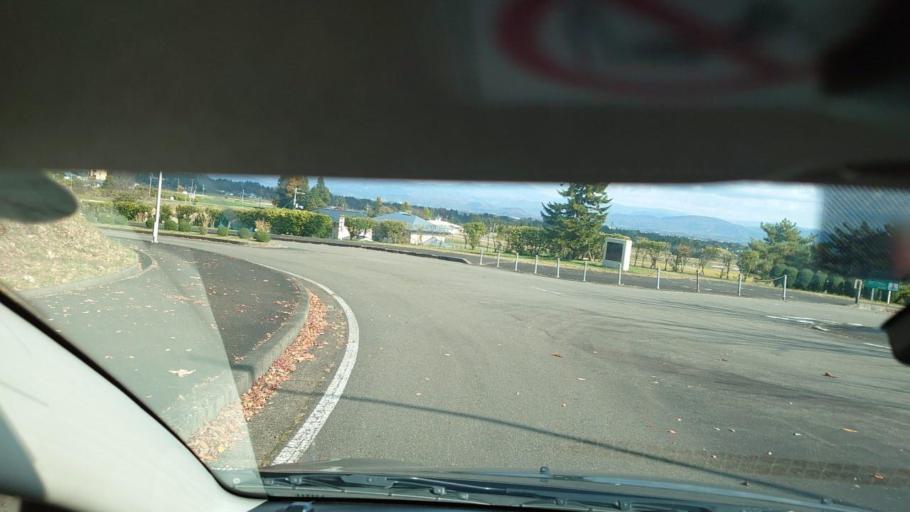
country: JP
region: Iwate
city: Hanamaki
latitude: 39.4335
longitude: 141.0591
